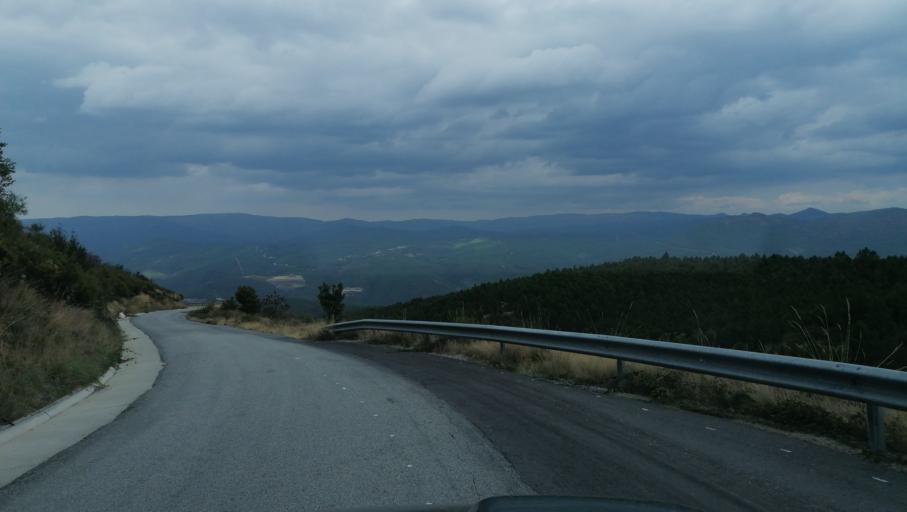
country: PT
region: Vila Real
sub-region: Vila Pouca de Aguiar
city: Vila Pouca de Aguiar
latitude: 41.5600
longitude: -7.6895
